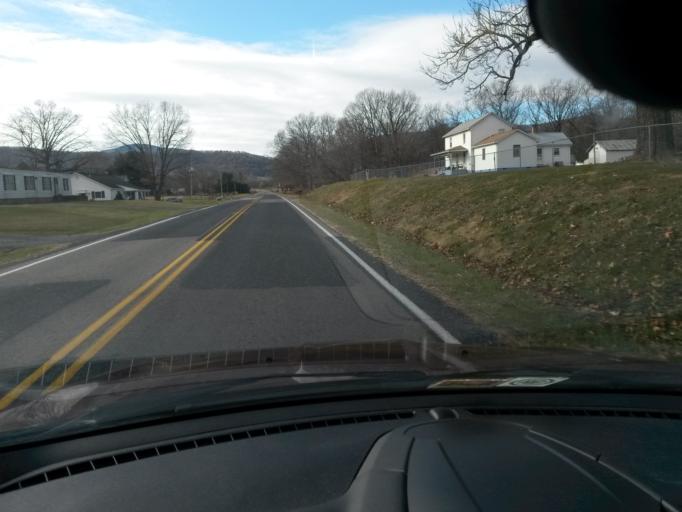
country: US
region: Virginia
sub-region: City of Staunton
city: Staunton
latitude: 38.2095
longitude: -79.2024
